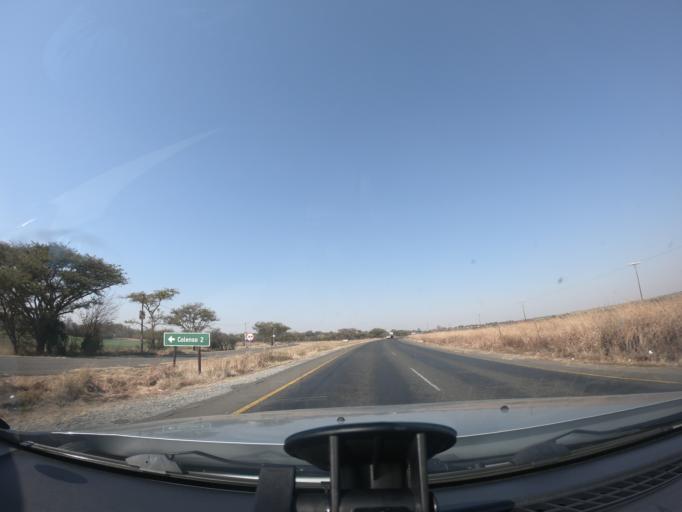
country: ZA
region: KwaZulu-Natal
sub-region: uThukela District Municipality
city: Ladysmith
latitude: -28.7361
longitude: 29.8165
